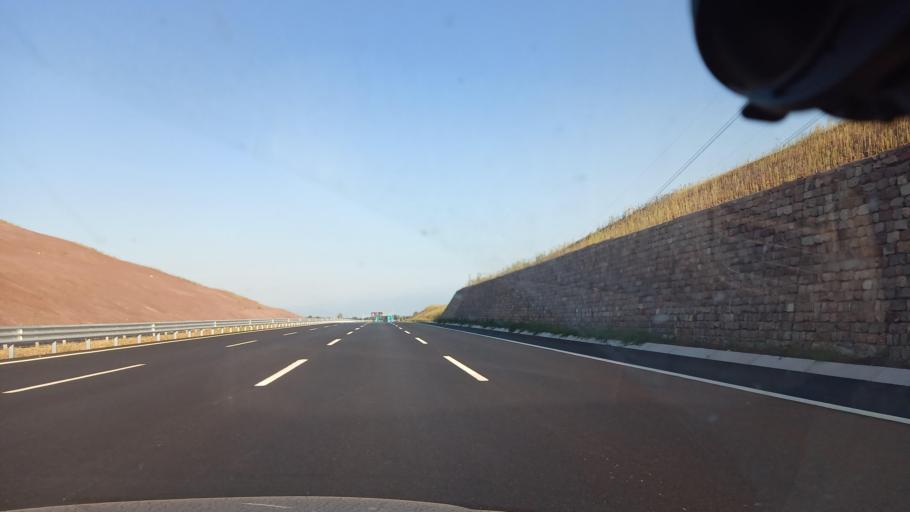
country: TR
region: Sakarya
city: Adapazari
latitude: 40.8217
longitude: 30.4041
